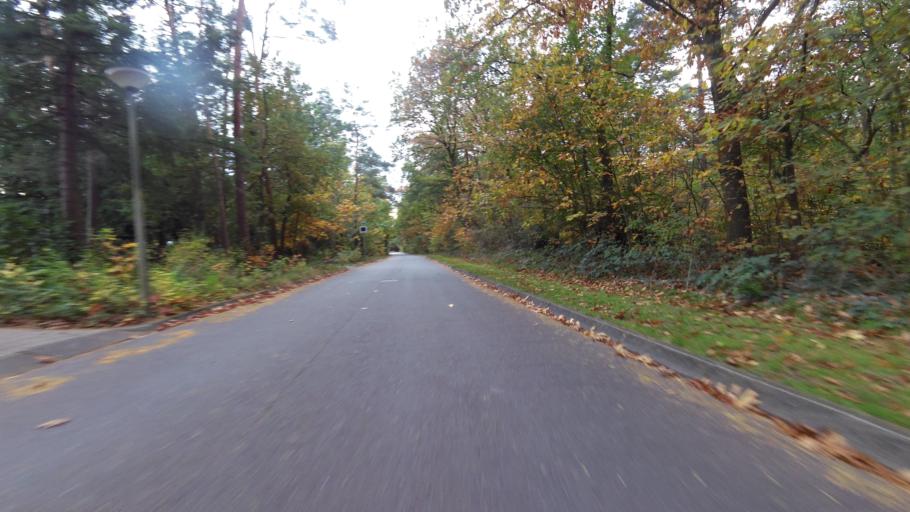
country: NL
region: Gelderland
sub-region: Gemeente Oldebroek
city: Oldebroek
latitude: 52.4108
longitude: 5.8814
